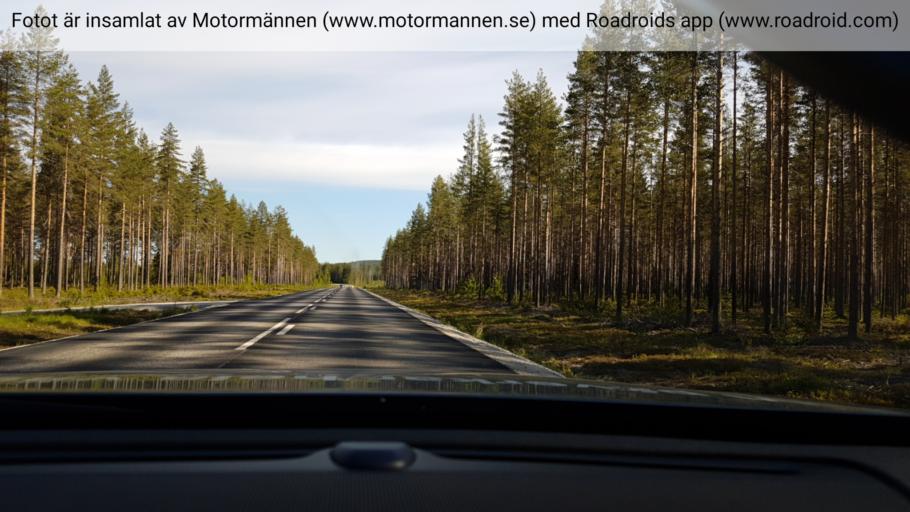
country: SE
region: Vaesterbotten
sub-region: Vindelns Kommun
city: Vindeln
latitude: 64.0745
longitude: 19.6339
